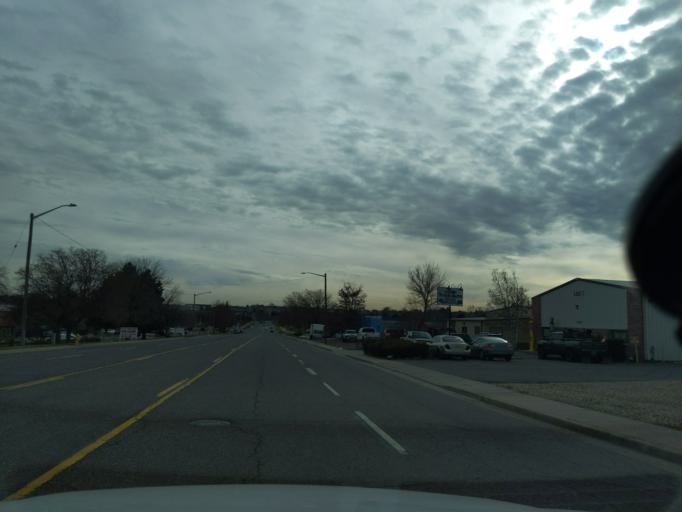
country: US
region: Colorado
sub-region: Adams County
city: Northglenn
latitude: 39.8927
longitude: -104.9660
